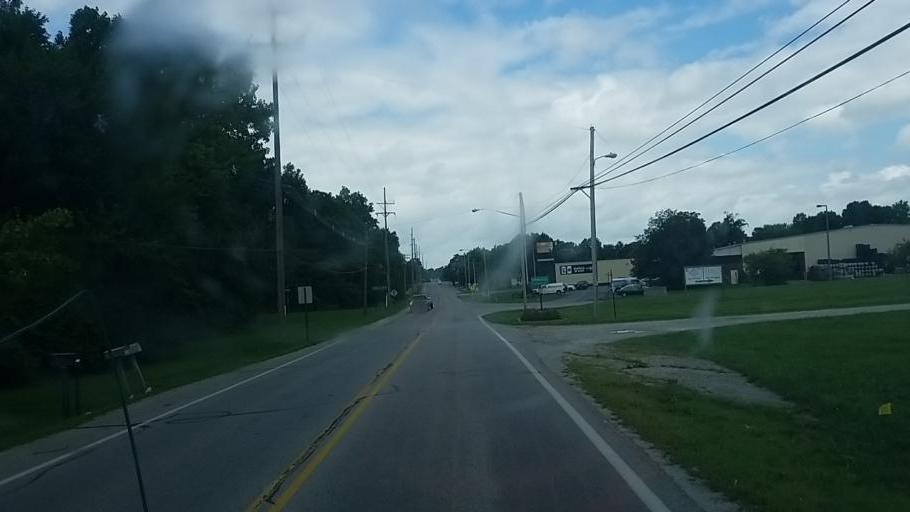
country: US
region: Ohio
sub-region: Clark County
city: Springfield
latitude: 39.8969
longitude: -83.7901
